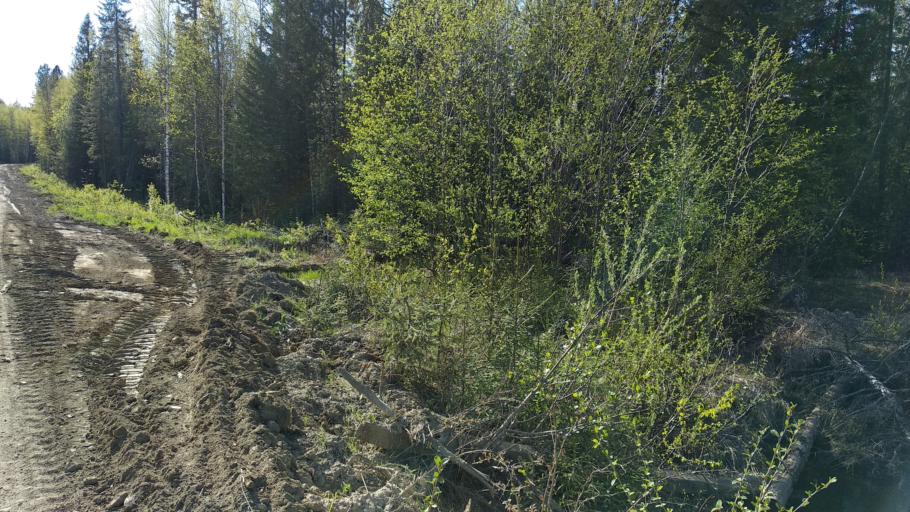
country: RU
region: Sverdlovsk
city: Karpinsk
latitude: 59.7006
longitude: 59.5397
